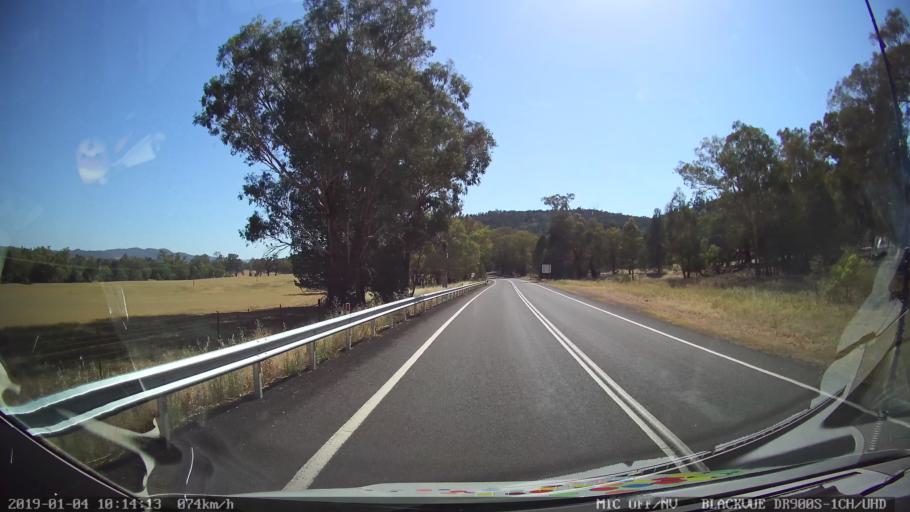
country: AU
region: New South Wales
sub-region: Cabonne
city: Canowindra
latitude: -33.3984
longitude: 148.4109
